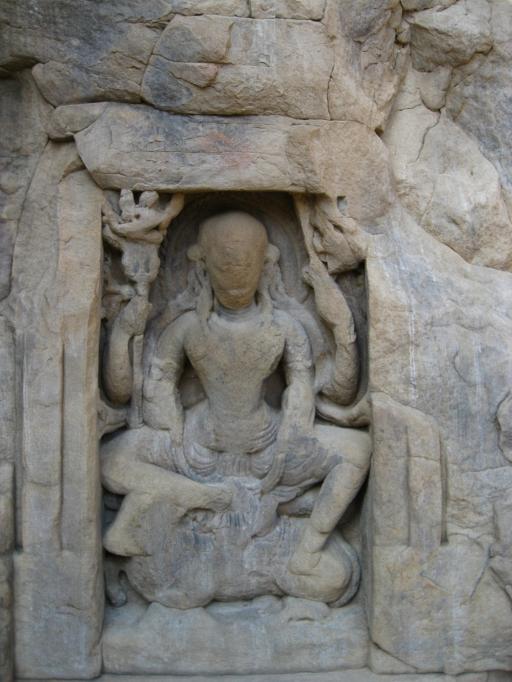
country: IN
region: Himachal Pradesh
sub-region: Kangra
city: Nagrota
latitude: 32.0729
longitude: 76.1371
